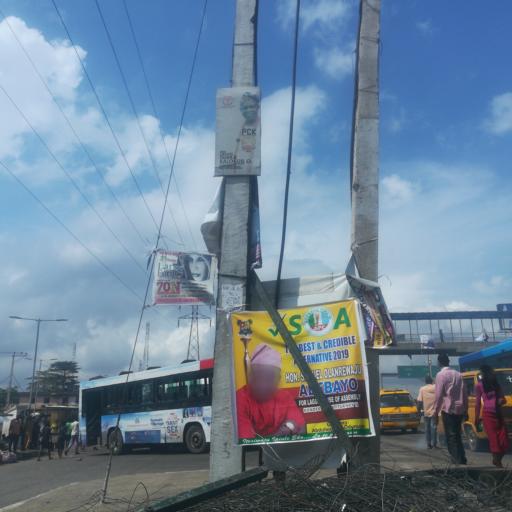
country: NG
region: Lagos
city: Ojota
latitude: 6.5984
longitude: 3.3870
